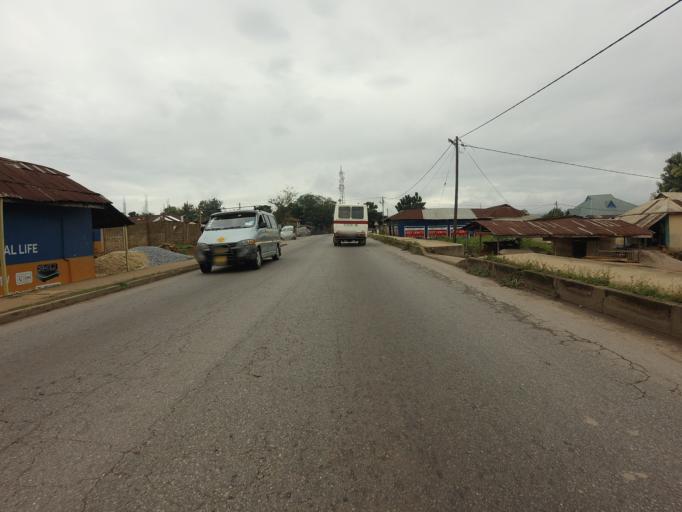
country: GH
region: Eastern
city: Begoro
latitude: 6.4341
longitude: -0.5849
